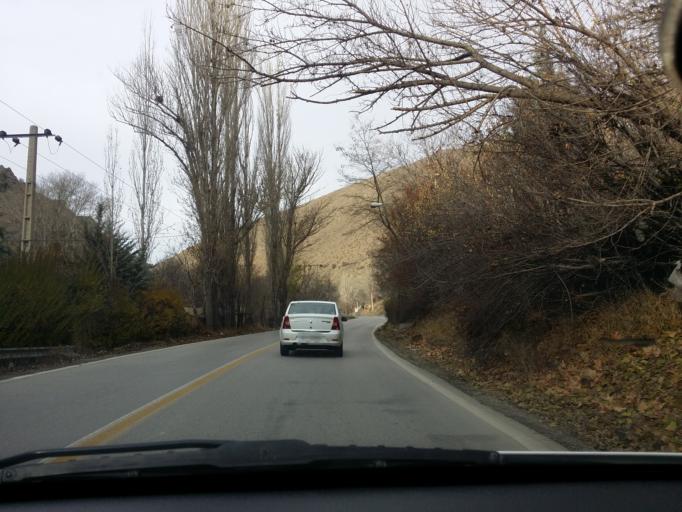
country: IR
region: Tehran
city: Tajrish
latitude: 36.0243
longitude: 51.2579
